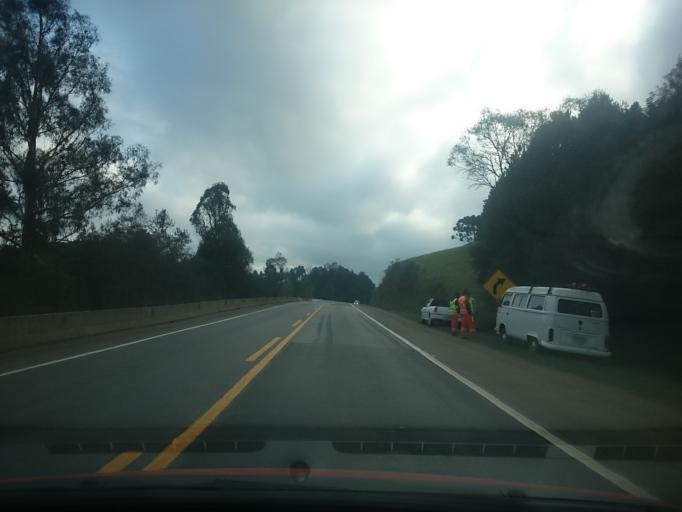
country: BR
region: Santa Catarina
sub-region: Lages
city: Lages
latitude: -27.9117
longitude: -50.4474
